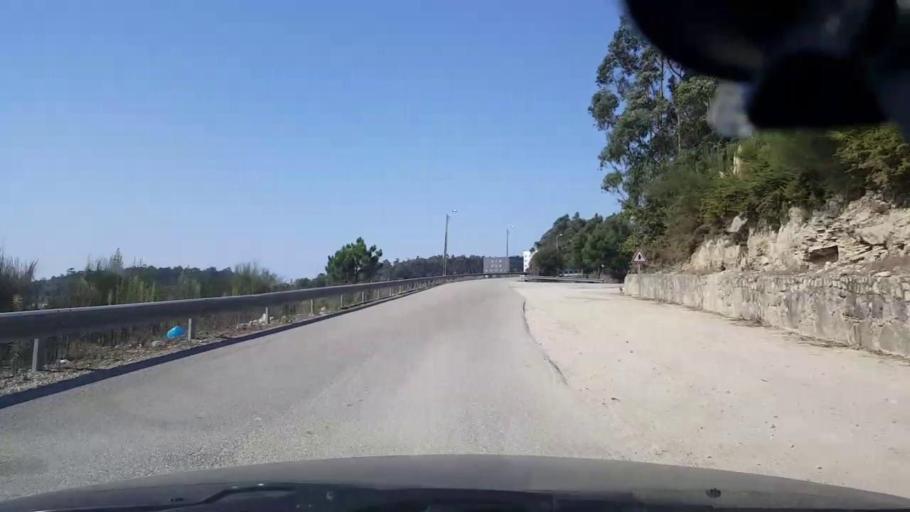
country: PT
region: Porto
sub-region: Vila do Conde
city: Vila do Conde
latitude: 41.3830
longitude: -8.7089
